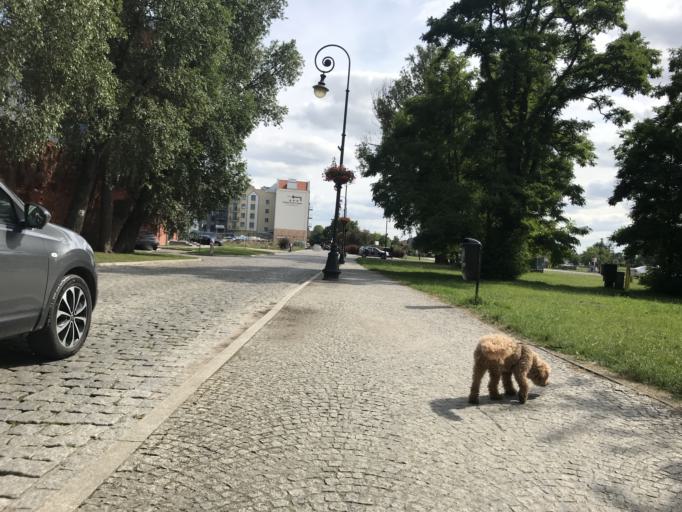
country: PL
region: Warmian-Masurian Voivodeship
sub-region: Powiat elblaski
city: Elblag
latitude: 54.1606
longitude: 19.3928
